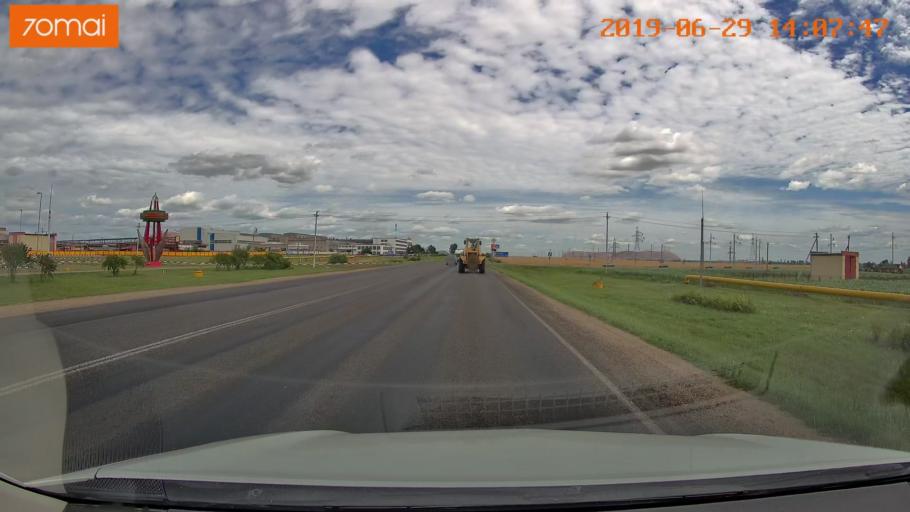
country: BY
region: Minsk
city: Salihorsk
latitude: 52.8530
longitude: 27.4716
